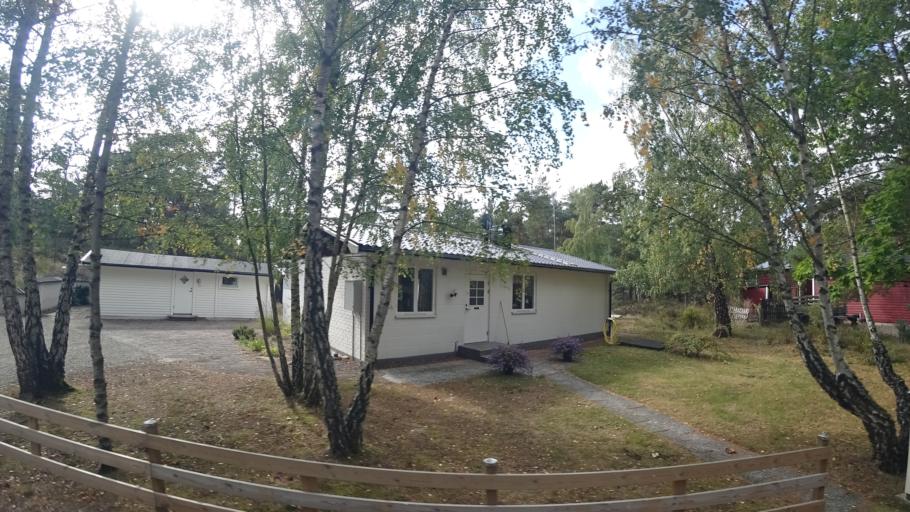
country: SE
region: Skane
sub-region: Kristianstads Kommun
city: Ahus
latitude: 55.9147
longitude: 14.2920
